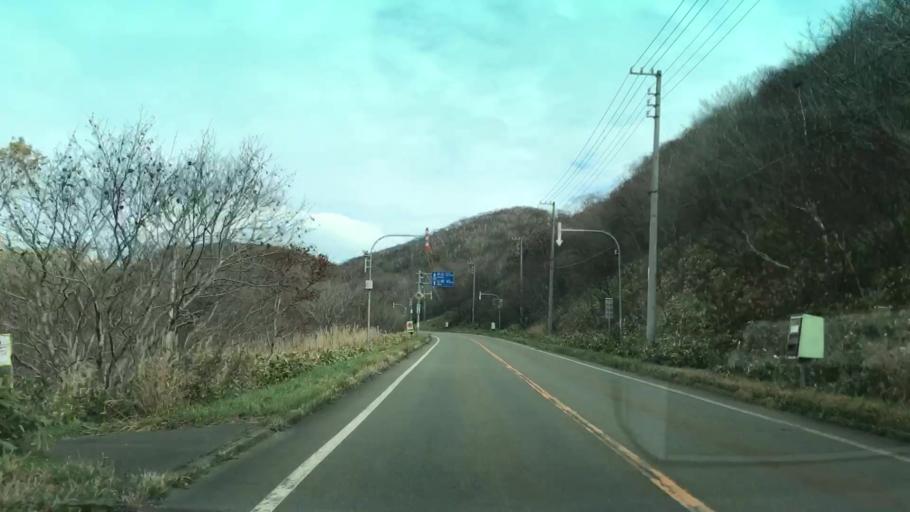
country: JP
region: Hokkaido
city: Obihiro
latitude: 42.0258
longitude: 143.2170
